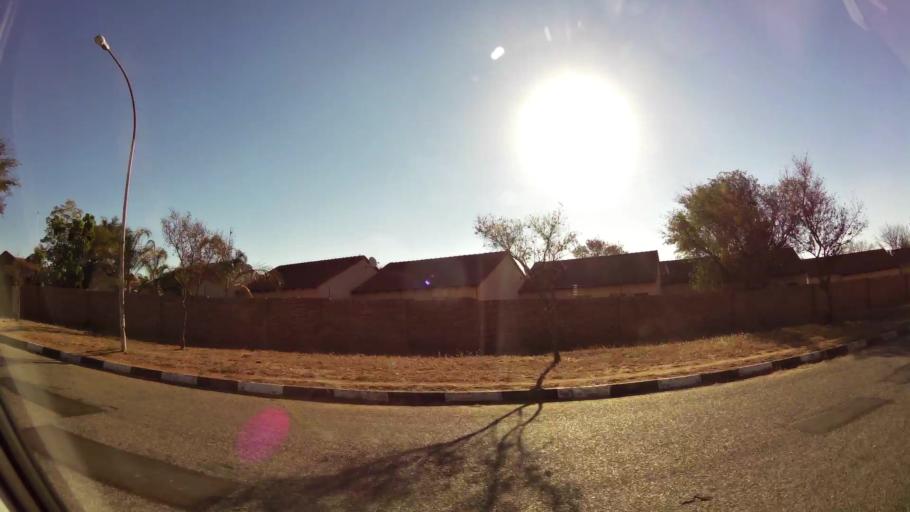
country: ZA
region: Limpopo
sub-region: Capricorn District Municipality
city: Polokwane
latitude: -23.8877
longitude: 29.4871
